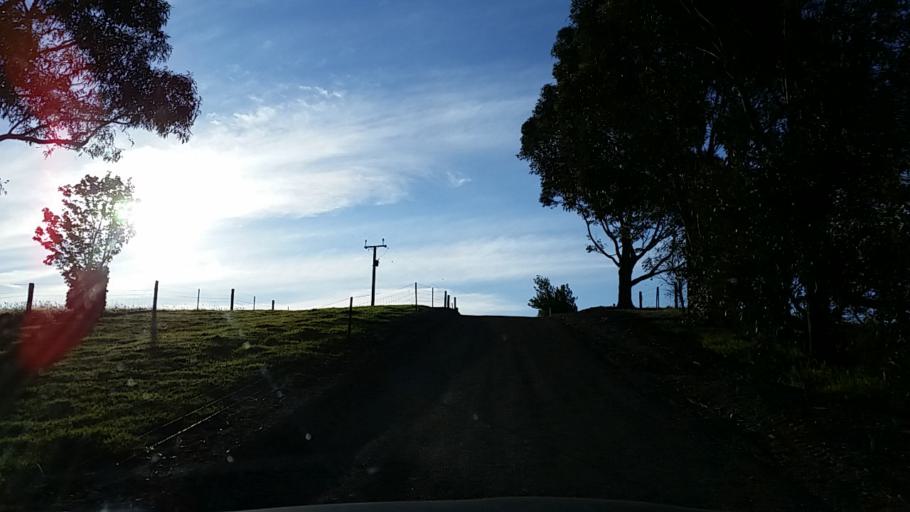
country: AU
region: South Australia
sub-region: Mount Barker
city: Meadows
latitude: -35.2403
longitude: 138.7564
